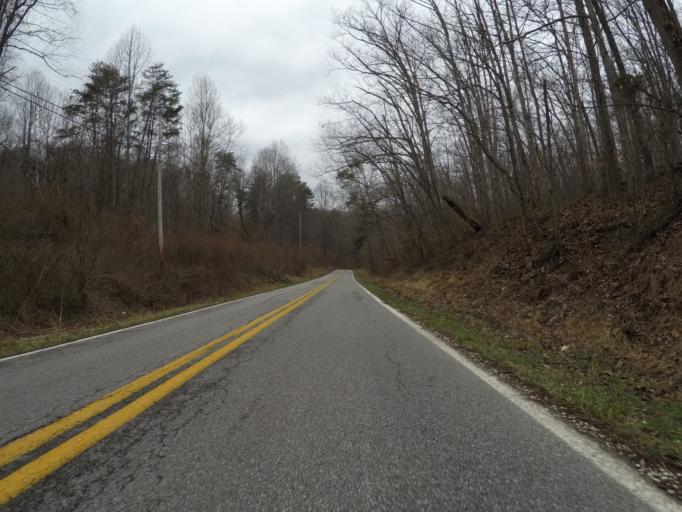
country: US
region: West Virginia
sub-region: Cabell County
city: Barboursville
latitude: 38.4386
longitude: -82.2447
